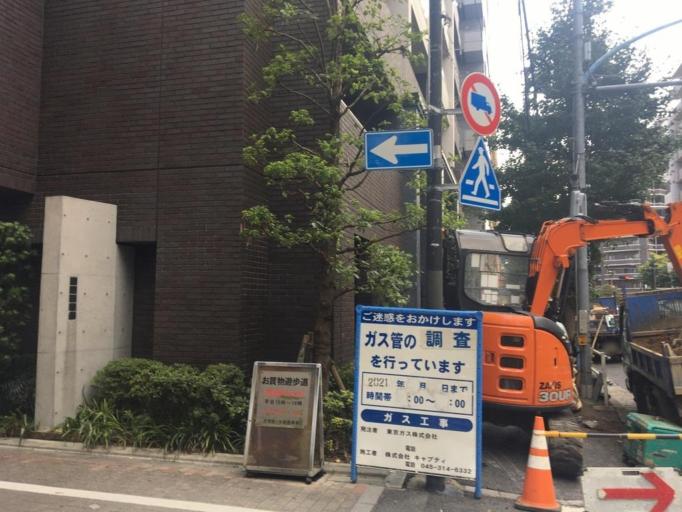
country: JP
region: Tokyo
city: Tokyo
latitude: 35.7084
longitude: 139.7313
